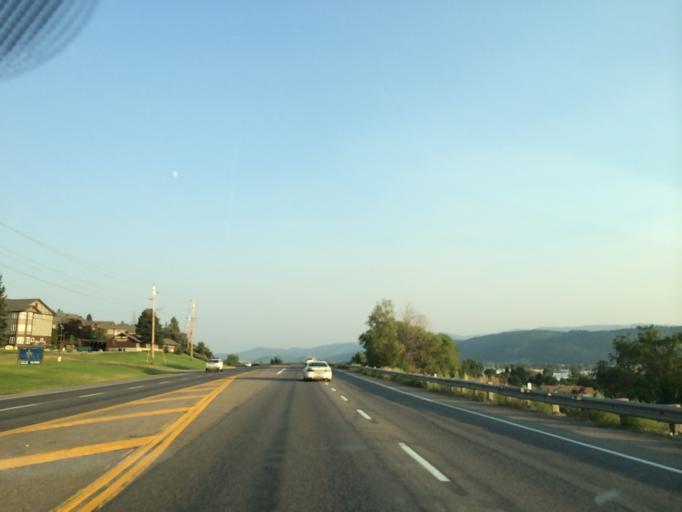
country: US
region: Montana
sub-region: Flathead County
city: Kalispell
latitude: 48.2124
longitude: -114.3277
